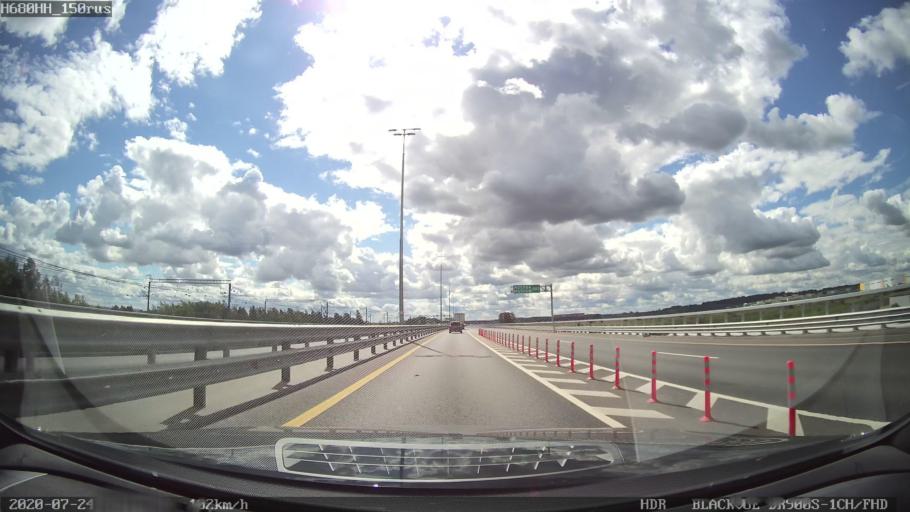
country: RU
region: St.-Petersburg
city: Shushary
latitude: 59.8022
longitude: 30.3379
